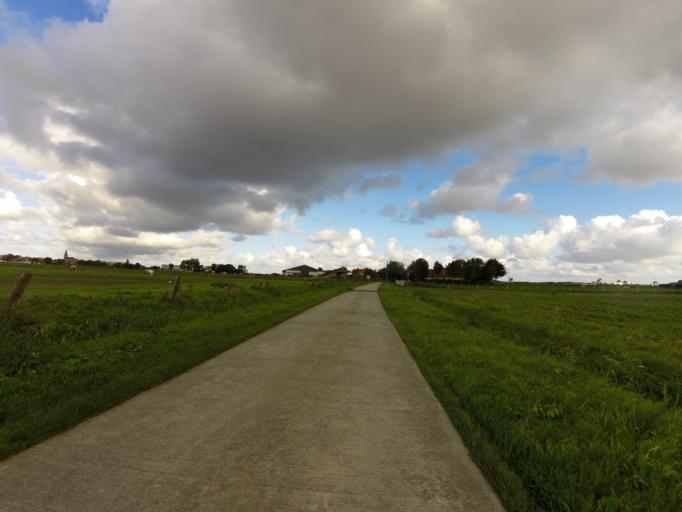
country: BE
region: Flanders
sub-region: Provincie West-Vlaanderen
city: Middelkerke
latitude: 51.1789
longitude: 2.8499
